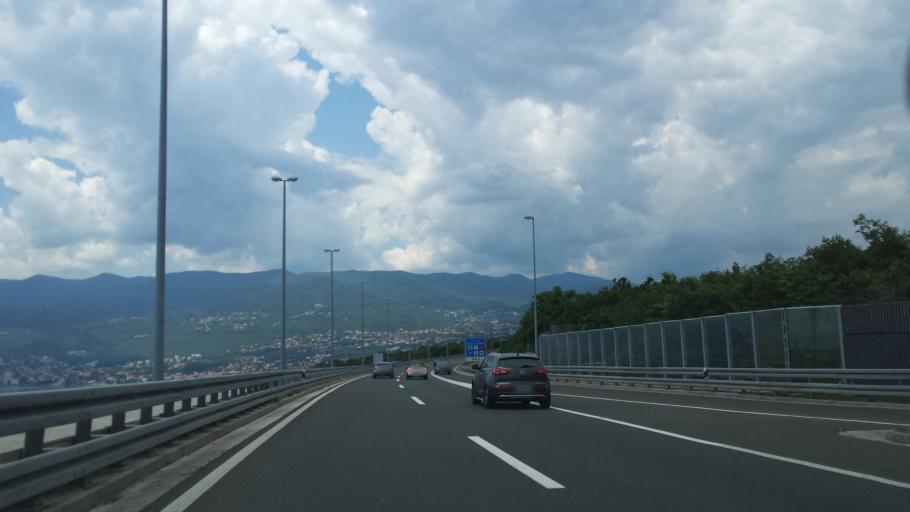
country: HR
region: Primorsko-Goranska
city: Rubesi
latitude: 45.3483
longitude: 14.3687
